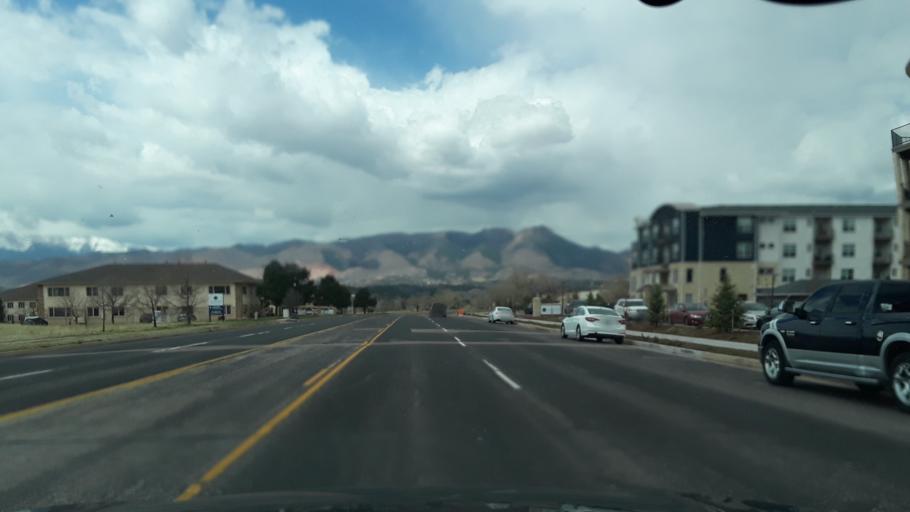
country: US
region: Colorado
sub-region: El Paso County
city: Air Force Academy
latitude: 38.9455
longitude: -104.8054
